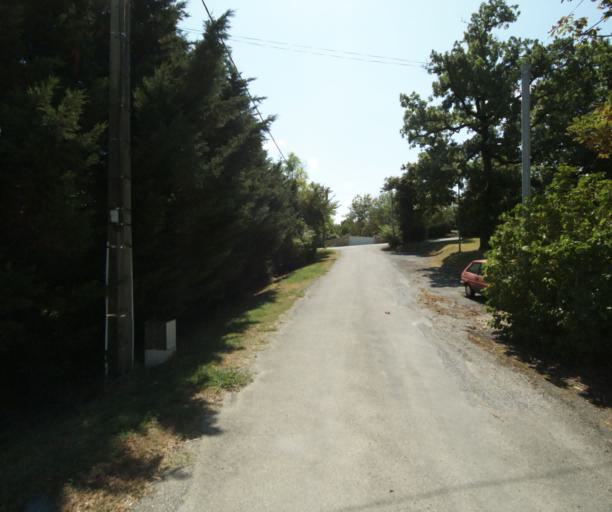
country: FR
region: Midi-Pyrenees
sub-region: Departement de la Haute-Garonne
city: Auriac-sur-Vendinelle
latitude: 43.4666
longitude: 1.7945
